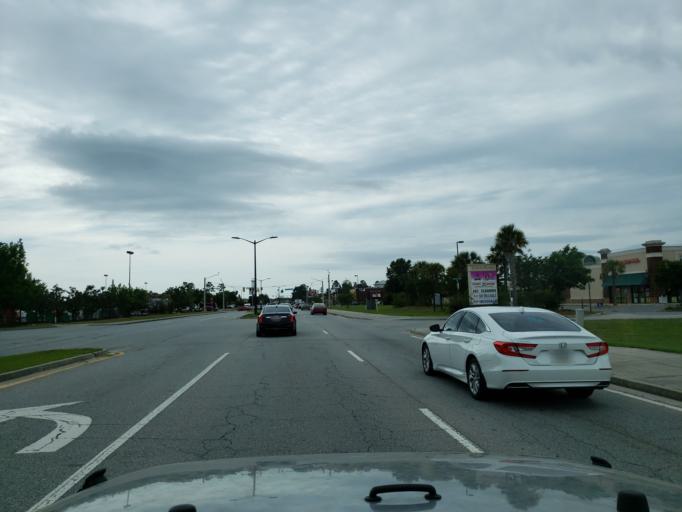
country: US
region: Georgia
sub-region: Chatham County
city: Pooler
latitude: 32.1446
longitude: -81.2475
